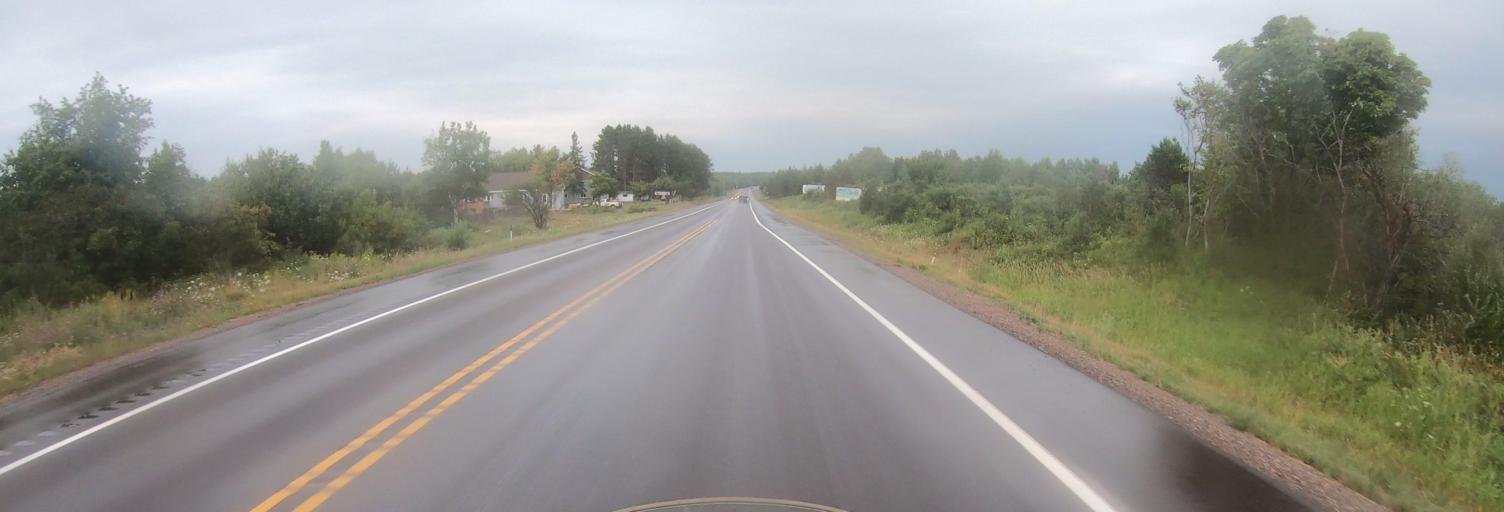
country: US
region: Michigan
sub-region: Houghton County
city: Hancock
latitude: 47.1455
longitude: -88.5676
